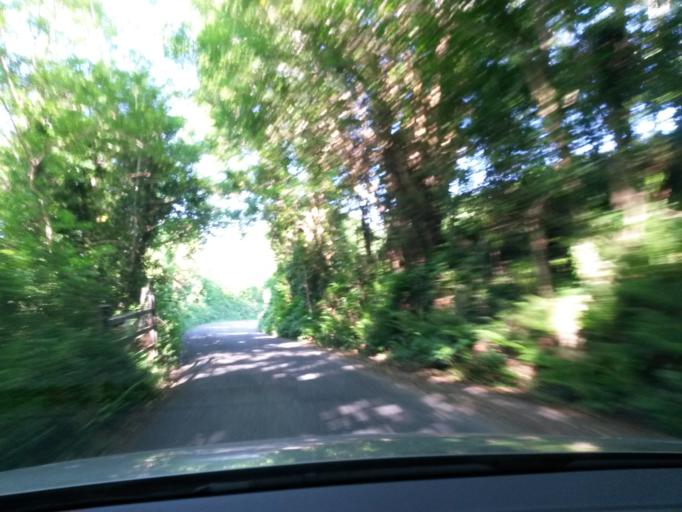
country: IE
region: Munster
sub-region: Ciarrai
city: Kenmare
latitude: 51.8014
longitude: -9.7645
